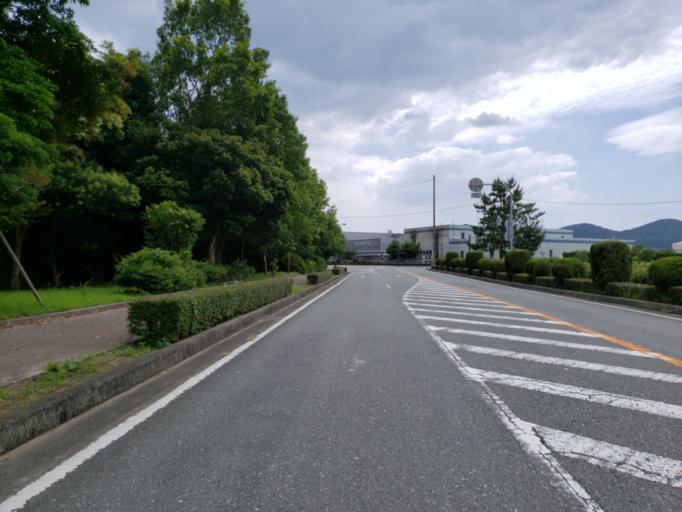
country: JP
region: Hyogo
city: Aioi
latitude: 34.7803
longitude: 134.4732
